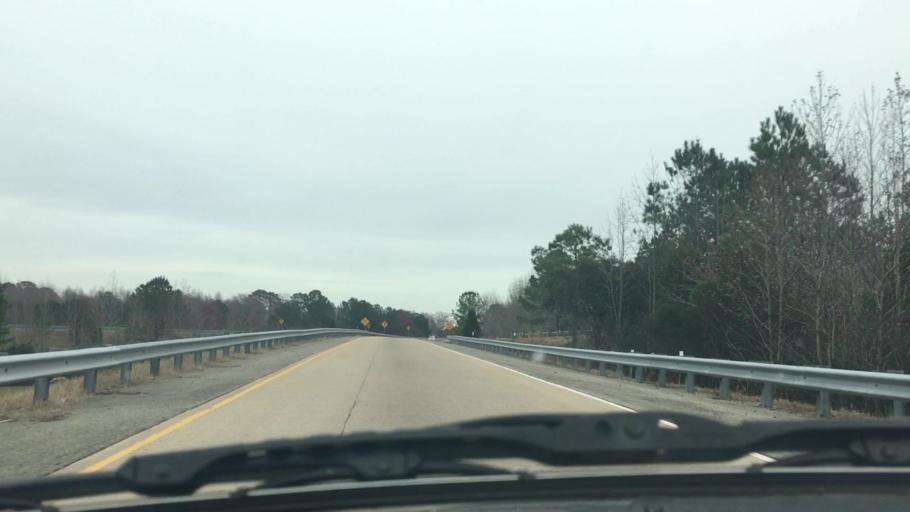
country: US
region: Virginia
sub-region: City of Portsmouth
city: Portsmouth Heights
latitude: 36.8659
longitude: -76.4300
